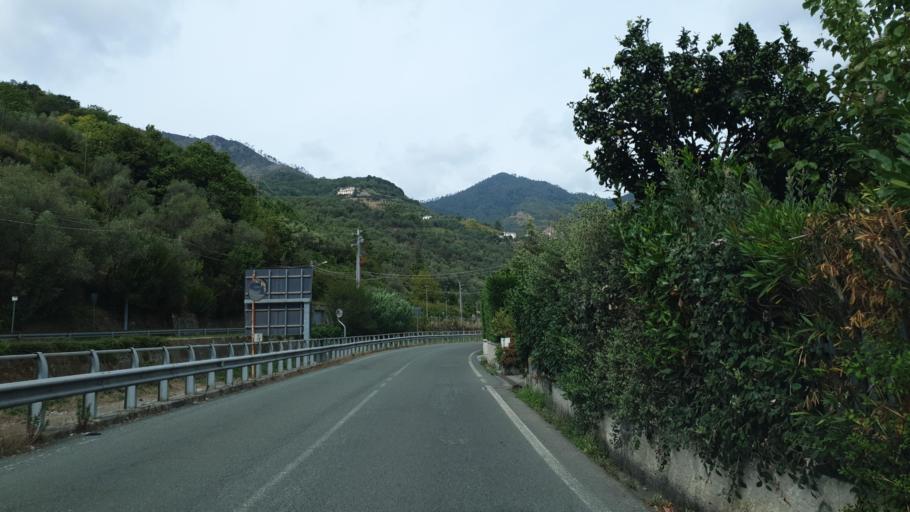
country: IT
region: Liguria
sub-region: Provincia di La Spezia
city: Levanto
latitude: 44.1801
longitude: 9.6227
